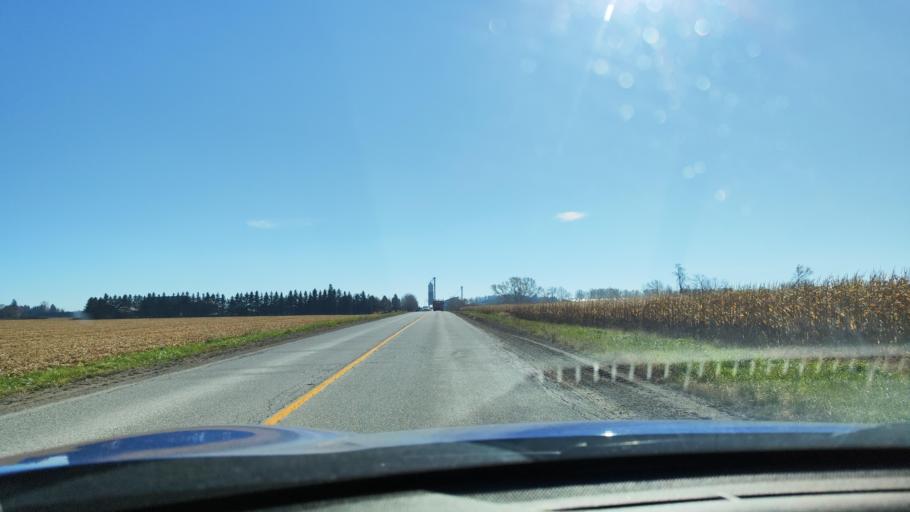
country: CA
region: Ontario
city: Wasaga Beach
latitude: 44.4452
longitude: -79.9997
